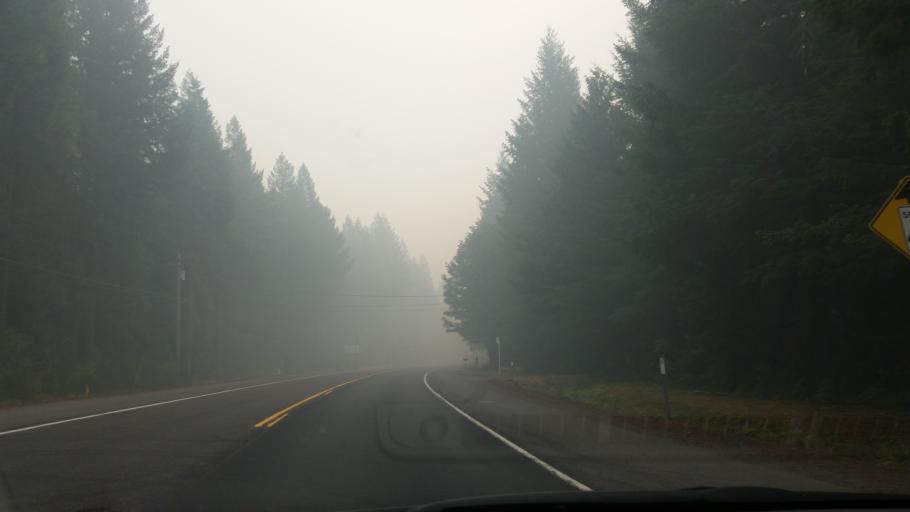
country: US
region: Oregon
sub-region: Lane County
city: Oakridge
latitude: 44.1769
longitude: -122.1707
